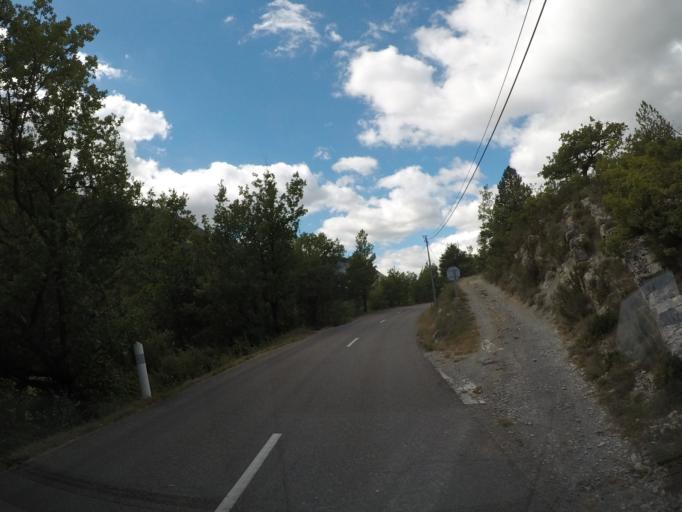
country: FR
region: Provence-Alpes-Cote d'Azur
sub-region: Departement des Hautes-Alpes
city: Laragne-Monteglin
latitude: 44.1739
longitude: 5.6989
